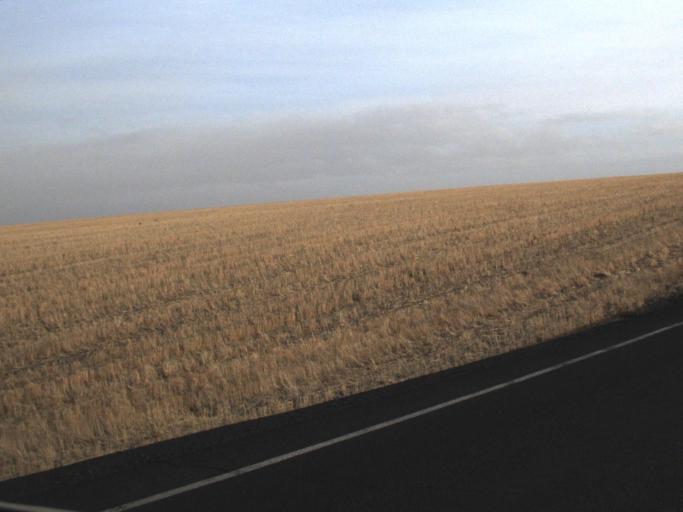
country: US
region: Washington
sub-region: Adams County
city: Ritzville
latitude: 47.2038
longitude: -118.6866
